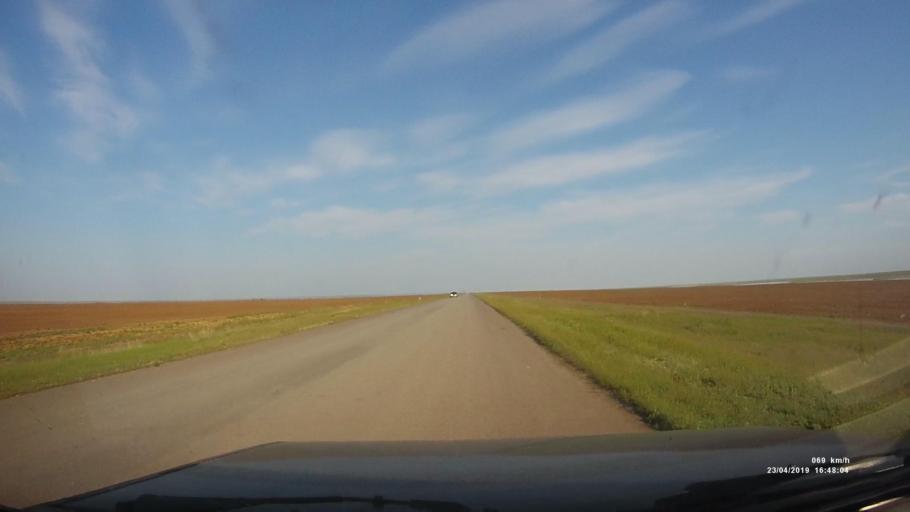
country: RU
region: Kalmykiya
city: Priyutnoye
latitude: 46.3364
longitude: 43.2565
